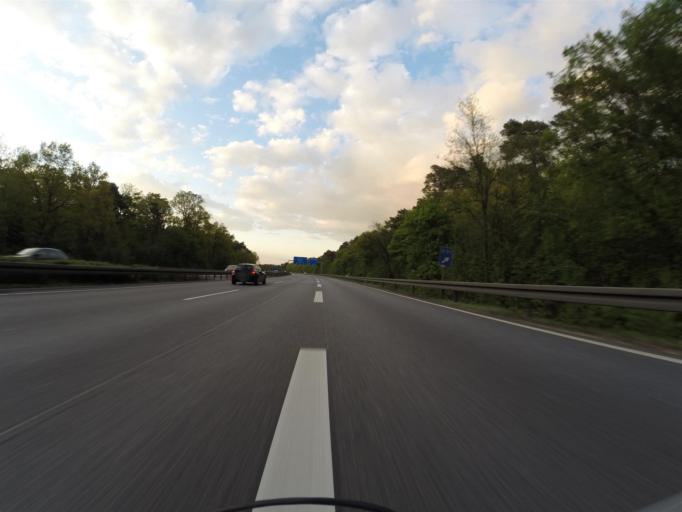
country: DE
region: Hesse
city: Raunheim
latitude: 50.0140
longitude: 8.4956
